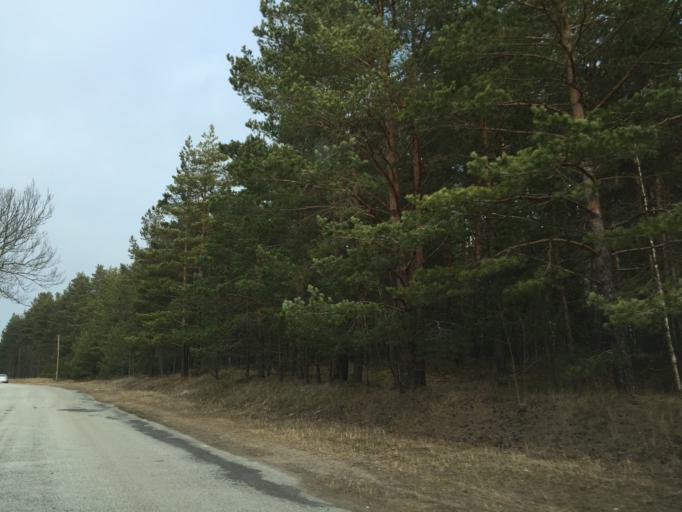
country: LV
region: Salacgrivas
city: Ainazi
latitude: 57.9327
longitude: 24.3920
